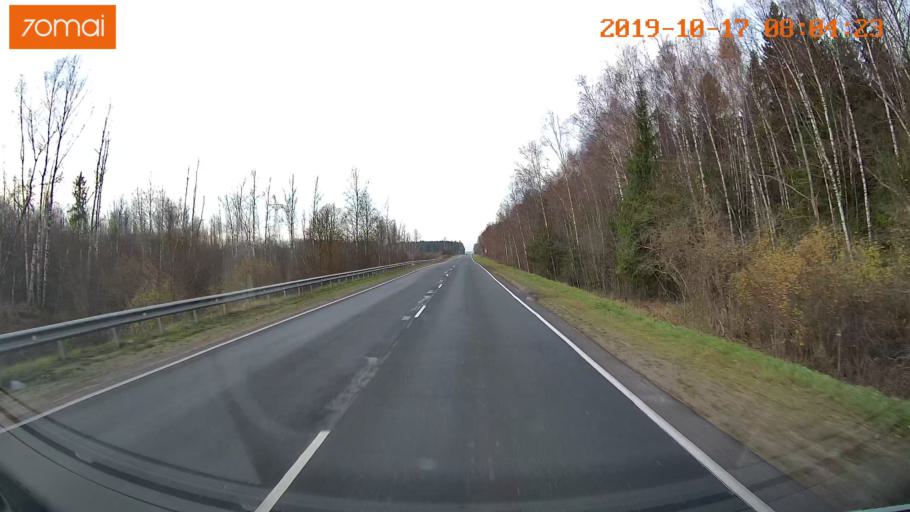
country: RU
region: Vladimir
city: Belaya Rechka
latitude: 56.3459
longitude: 39.4360
